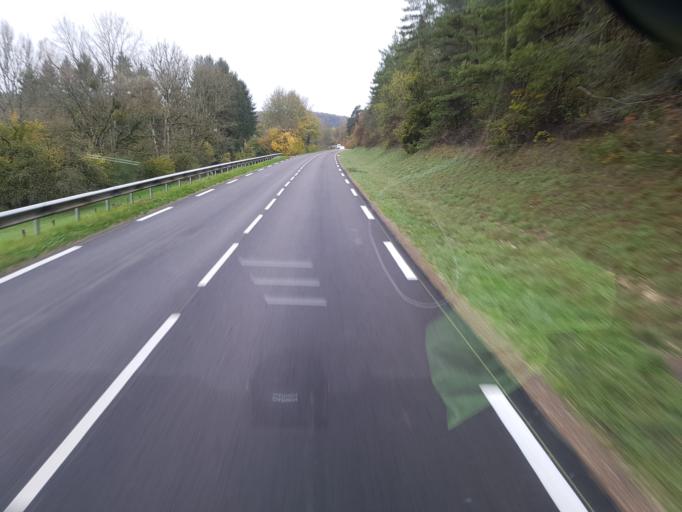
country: FR
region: Bourgogne
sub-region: Departement de la Cote-d'Or
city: Messigny-et-Vantoux
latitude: 47.5404
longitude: 4.9476
